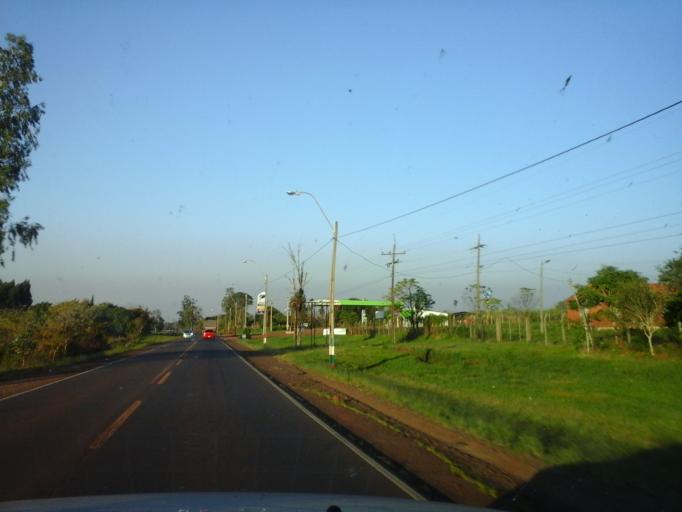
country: PY
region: Itapua
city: General Delgado
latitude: -27.0896
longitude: -56.5109
